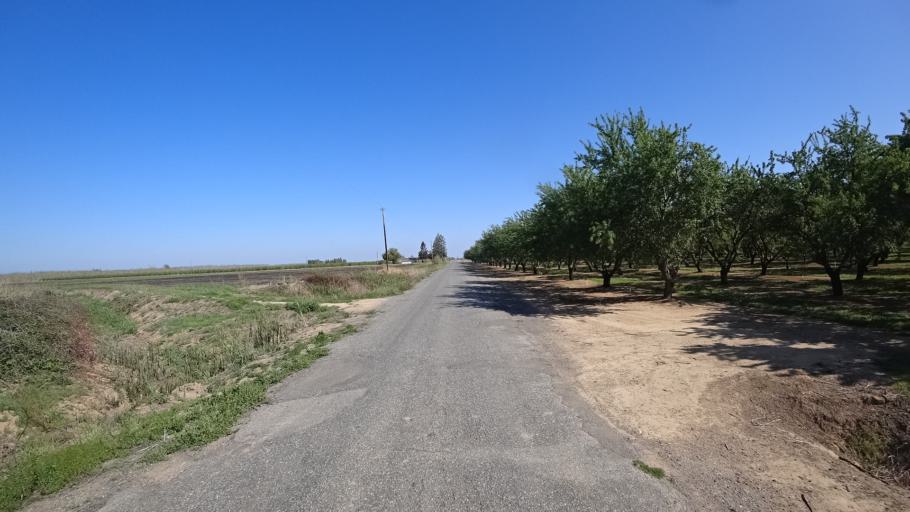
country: US
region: California
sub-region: Glenn County
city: Hamilton City
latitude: 39.6500
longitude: -122.0180
